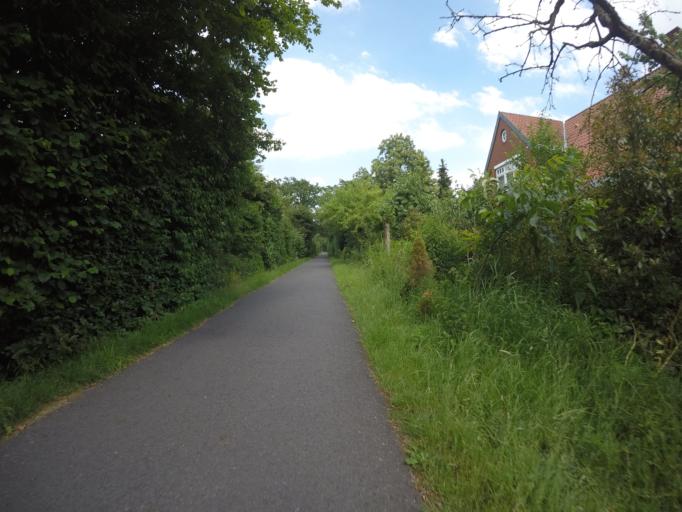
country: DE
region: North Rhine-Westphalia
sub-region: Regierungsbezirk Munster
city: Borken
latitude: 51.8467
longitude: 6.8410
